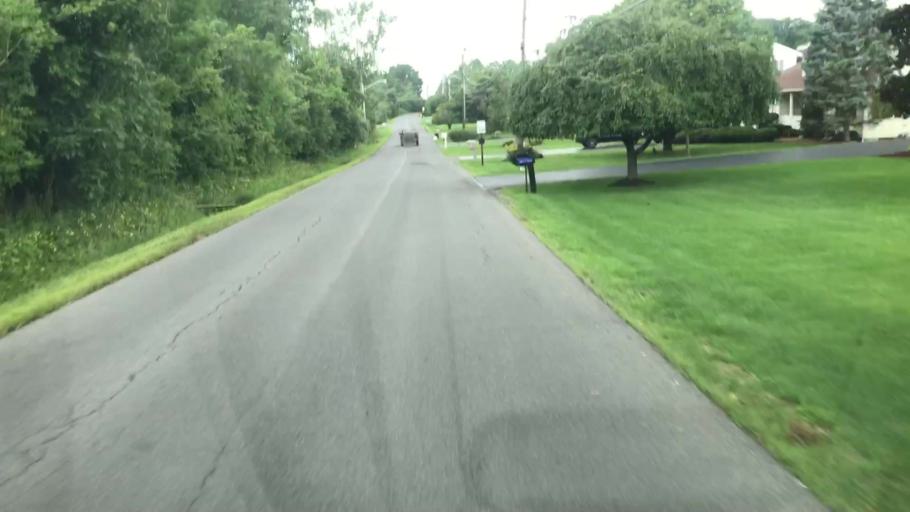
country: US
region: New York
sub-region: Cayuga County
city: Melrose Park
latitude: 42.9125
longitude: -76.5313
